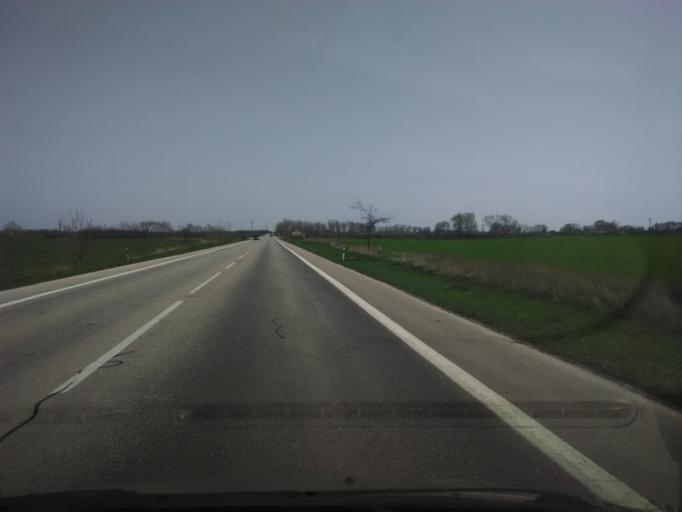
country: SK
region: Nitriansky
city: Sellye
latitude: 48.1430
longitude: 17.9833
